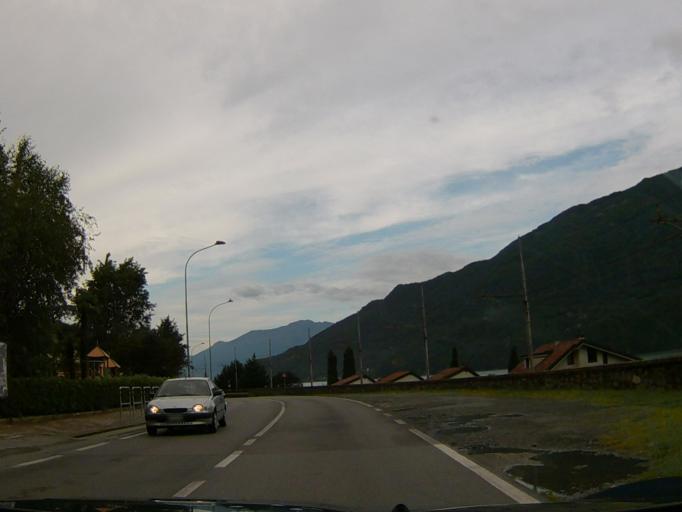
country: IT
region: Lombardy
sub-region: Provincia di Sondrio
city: Verceia
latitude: 46.2012
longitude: 9.4538
